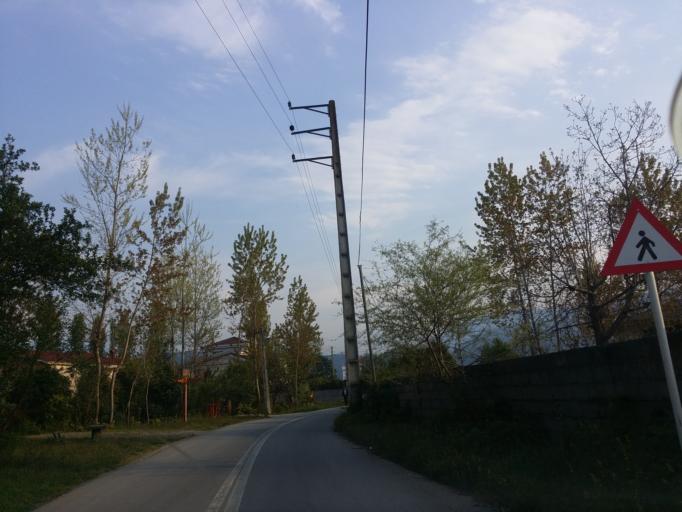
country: IR
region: Mazandaran
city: Chalus
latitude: 36.6834
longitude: 51.3719
